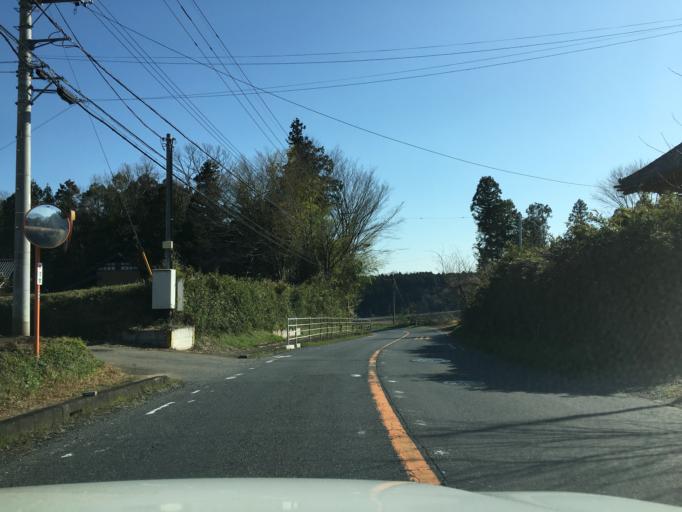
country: JP
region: Ibaraki
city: Omiya
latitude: 36.4562
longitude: 140.4071
